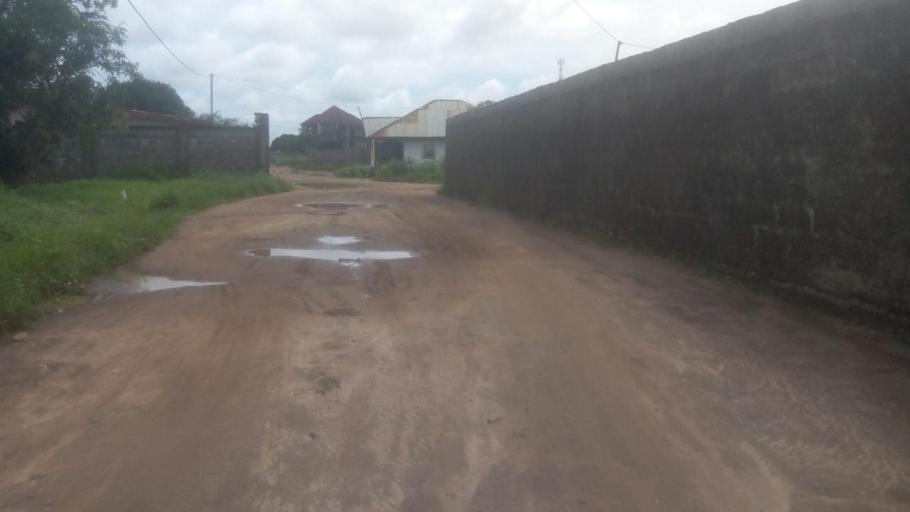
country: SL
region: Northern Province
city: Masoyila
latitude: 8.5980
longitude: -13.1874
